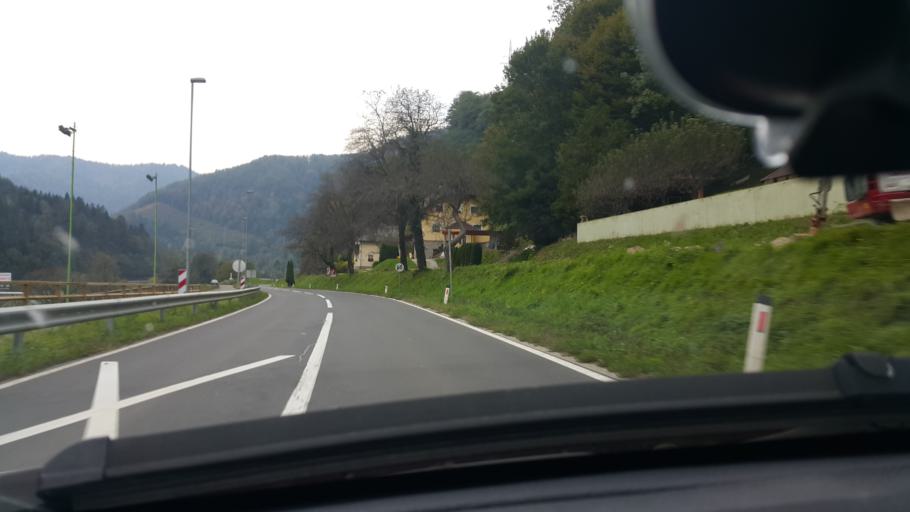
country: SI
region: Lovrenc na Pohorju
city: Lovrenc na Pohorju
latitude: 46.5843
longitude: 15.3849
